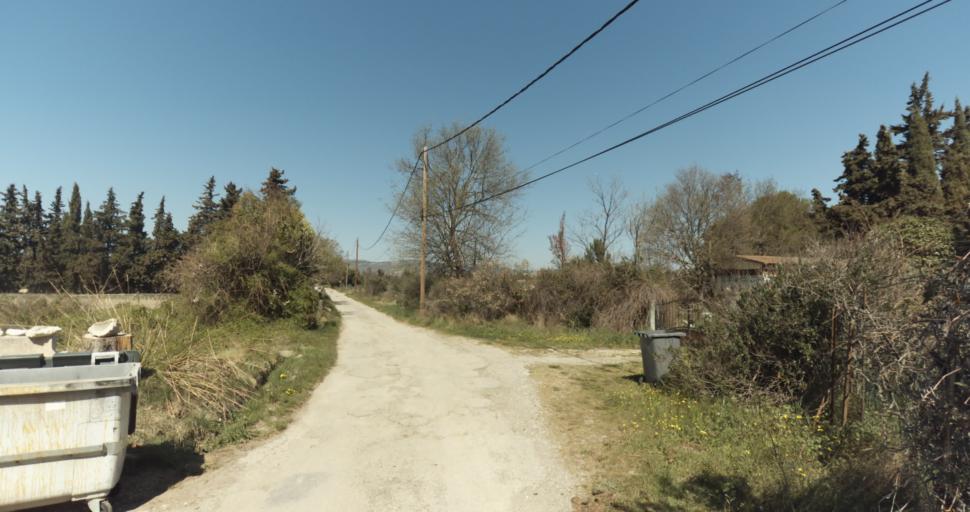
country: FR
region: Provence-Alpes-Cote d'Azur
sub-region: Departement des Bouches-du-Rhone
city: Pelissanne
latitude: 43.6169
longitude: 5.1518
